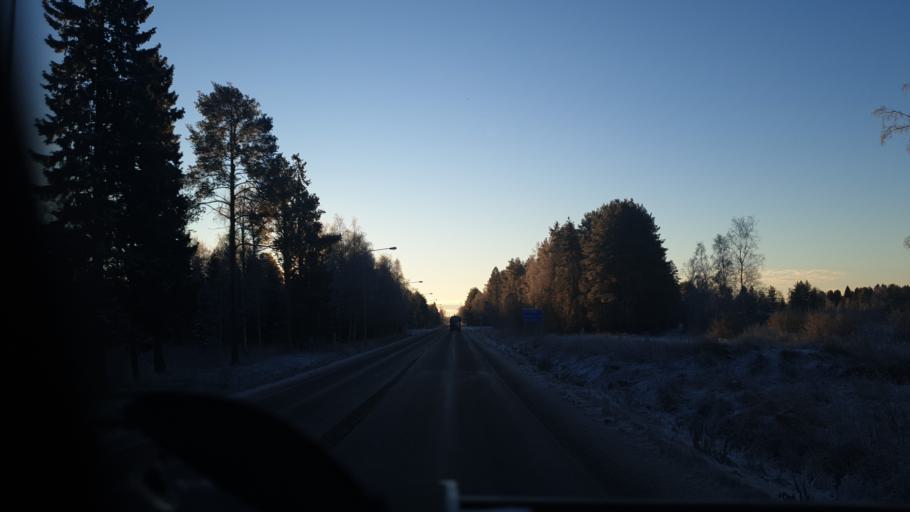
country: FI
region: Northern Ostrobothnia
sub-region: Ylivieska
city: Kalajoki
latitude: 64.2747
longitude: 23.9488
